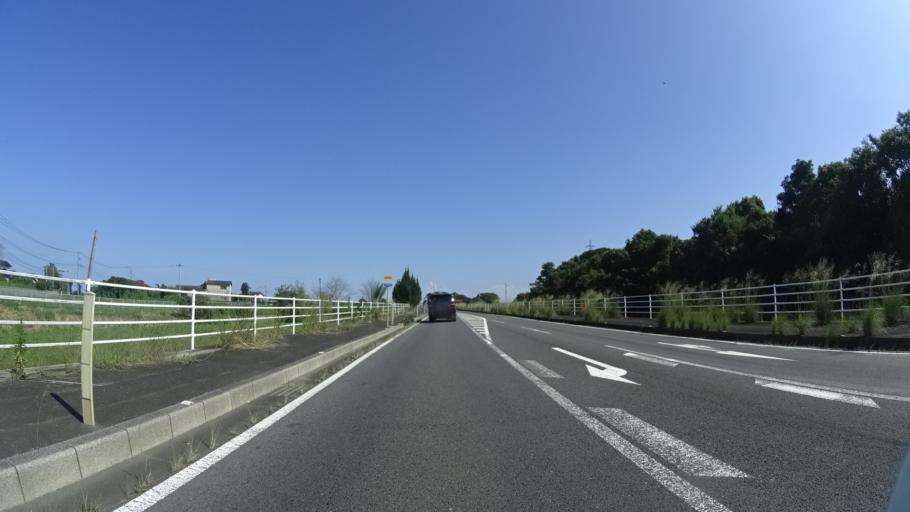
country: JP
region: Fukuoka
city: Tsuiki
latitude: 33.6714
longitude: 131.0181
